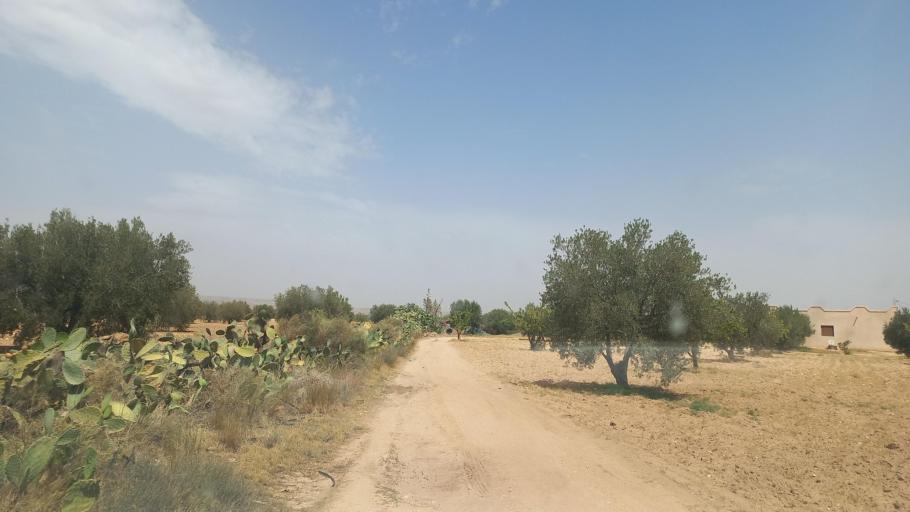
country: TN
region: Al Qasrayn
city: Kasserine
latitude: 35.2565
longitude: 9.0059
